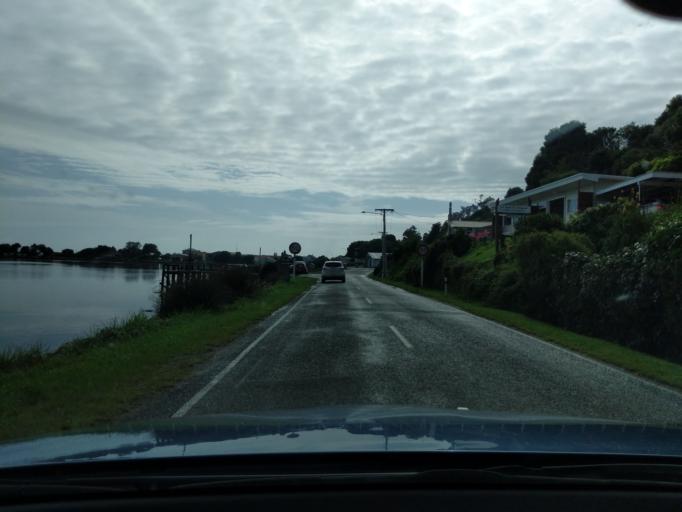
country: NZ
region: Tasman
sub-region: Tasman District
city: Takaka
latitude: -40.6795
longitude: 172.6785
